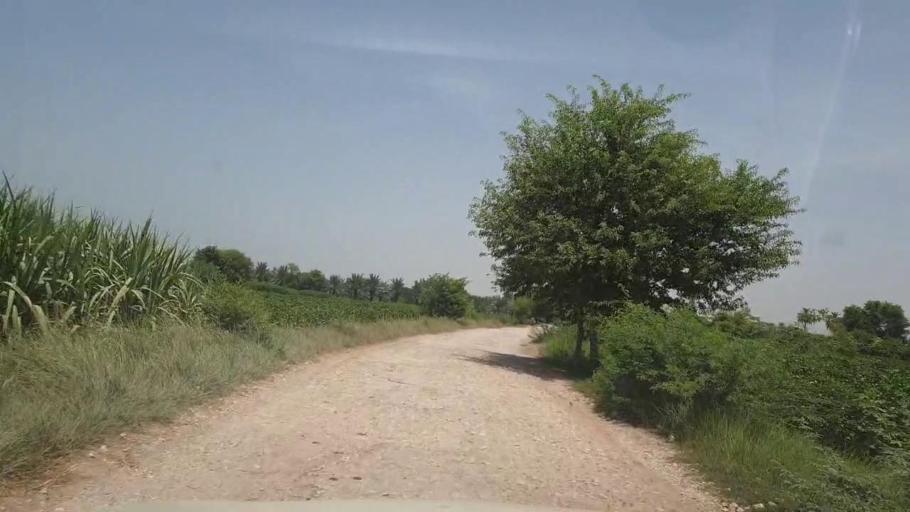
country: PK
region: Sindh
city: Bozdar
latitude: 27.1728
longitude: 68.6270
